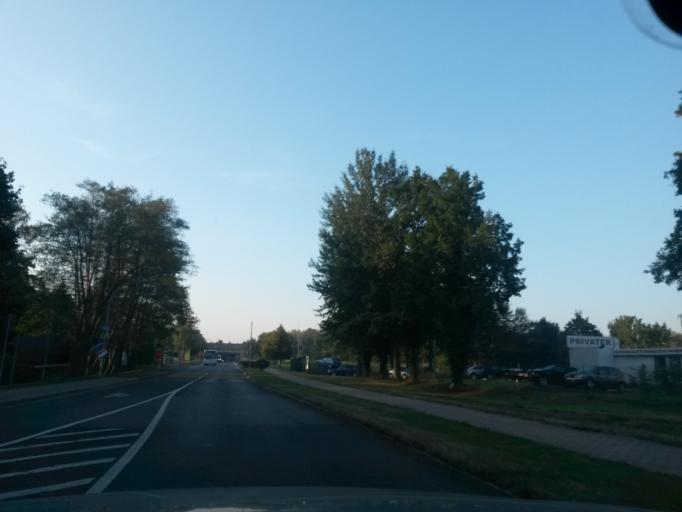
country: DE
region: Thuringia
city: Hermsdorf
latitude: 50.8839
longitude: 11.8492
